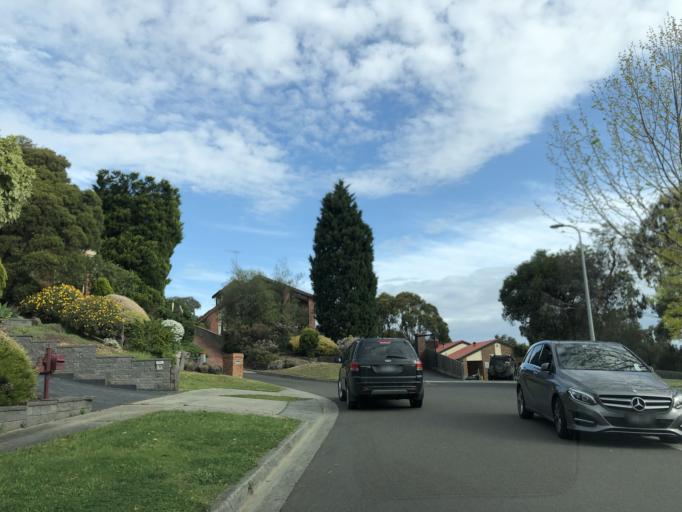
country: AU
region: Victoria
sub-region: Knox
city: Rowville
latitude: -37.9363
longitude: 145.2196
